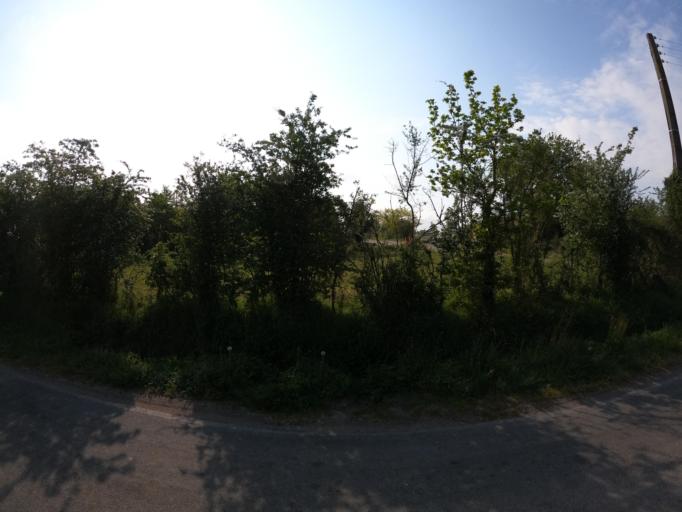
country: FR
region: Pays de la Loire
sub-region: Departement de Maine-et-Loire
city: Torfou
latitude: 47.0417
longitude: -1.1113
